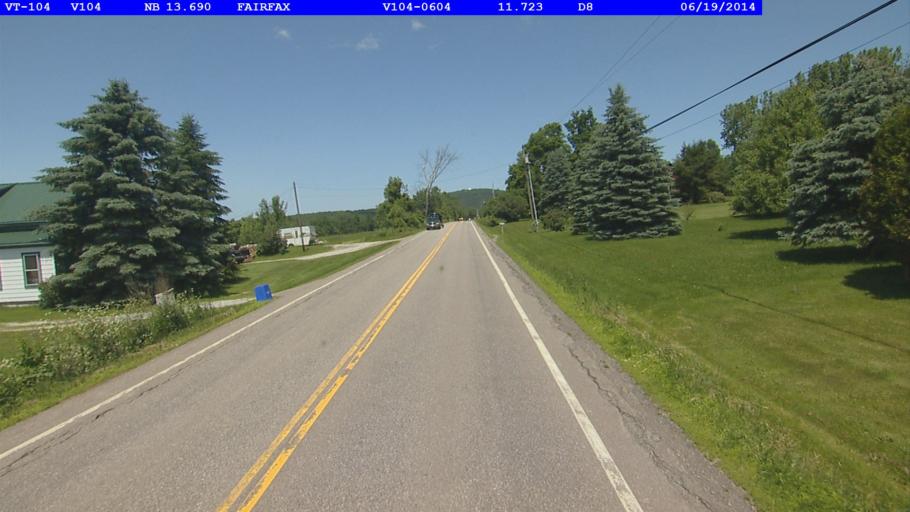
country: US
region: Vermont
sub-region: Franklin County
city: Saint Albans
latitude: 44.7527
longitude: -73.0547
